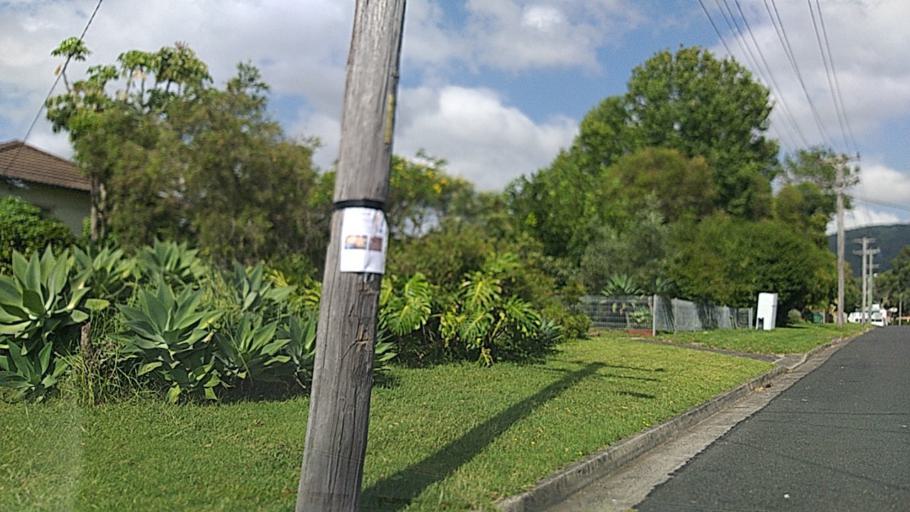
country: AU
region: New South Wales
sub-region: Wollongong
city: Corrimal
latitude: -34.3793
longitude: 150.8926
